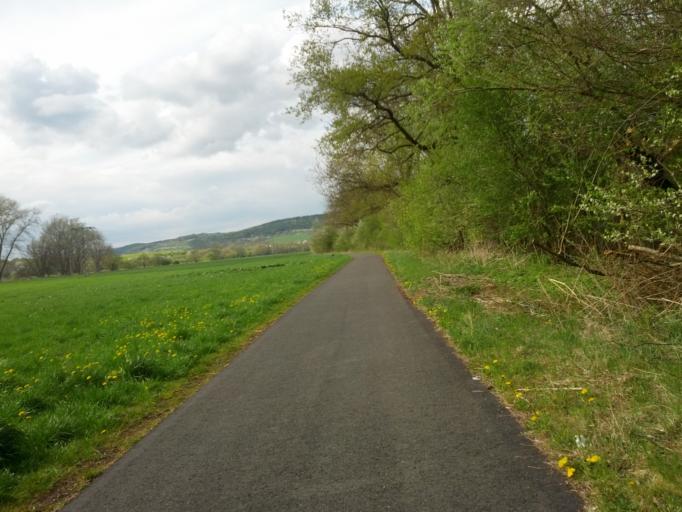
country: DE
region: Thuringia
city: Creuzburg
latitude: 51.0329
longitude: 10.2293
